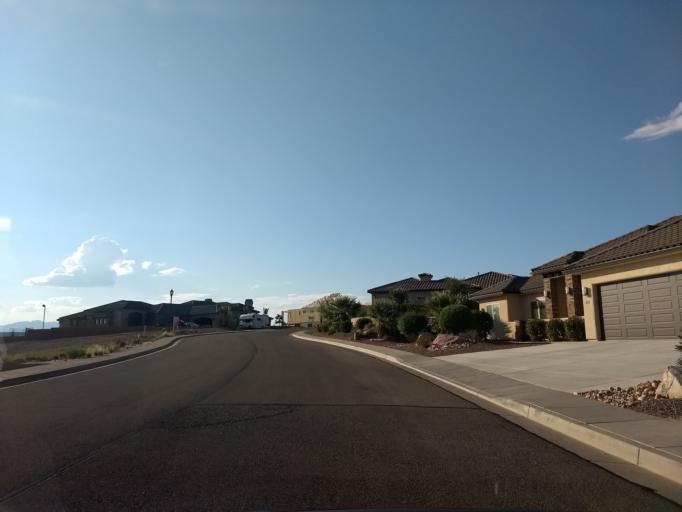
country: US
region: Utah
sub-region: Washington County
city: Saint George
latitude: 37.1008
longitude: -113.5474
